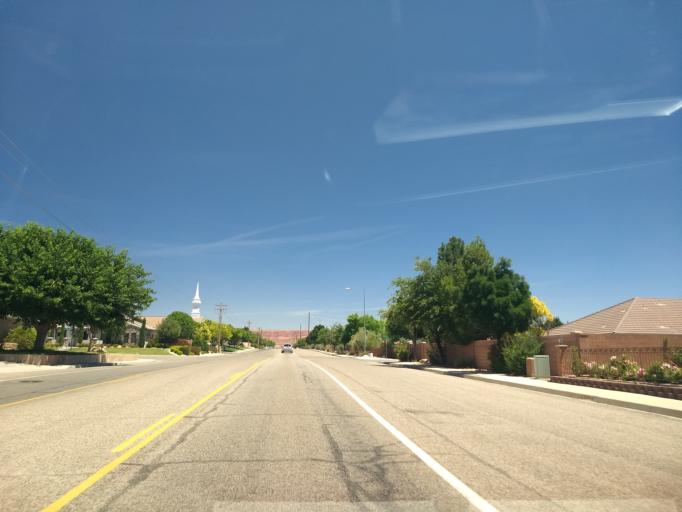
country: US
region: Utah
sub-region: Washington County
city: Saint George
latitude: 37.0668
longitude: -113.5432
